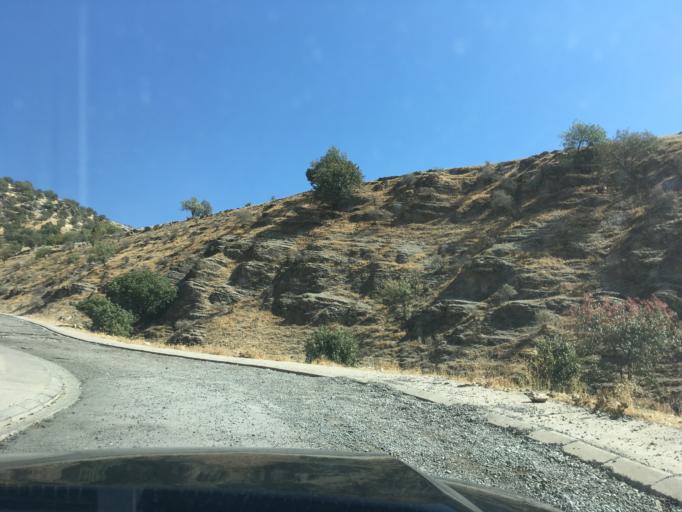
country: IQ
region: Arbil
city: Mergasur
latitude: 36.8315
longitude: 44.2153
